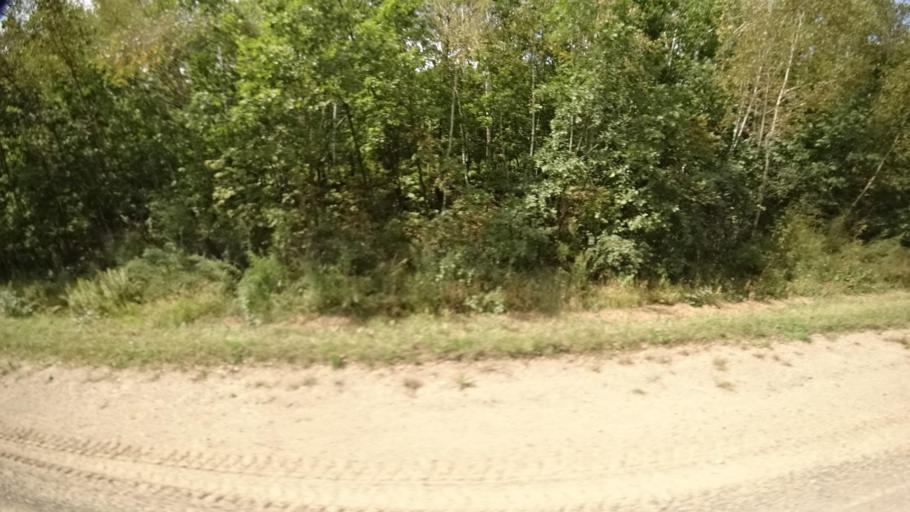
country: RU
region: Primorskiy
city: Yakovlevka
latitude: 44.6582
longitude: 133.5966
